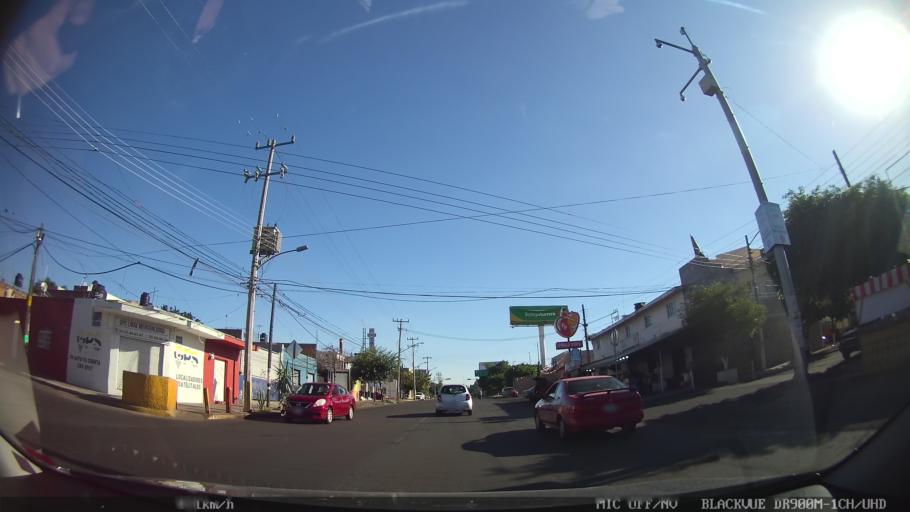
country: MX
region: Jalisco
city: Tlaquepaque
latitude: 20.6967
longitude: -103.3214
